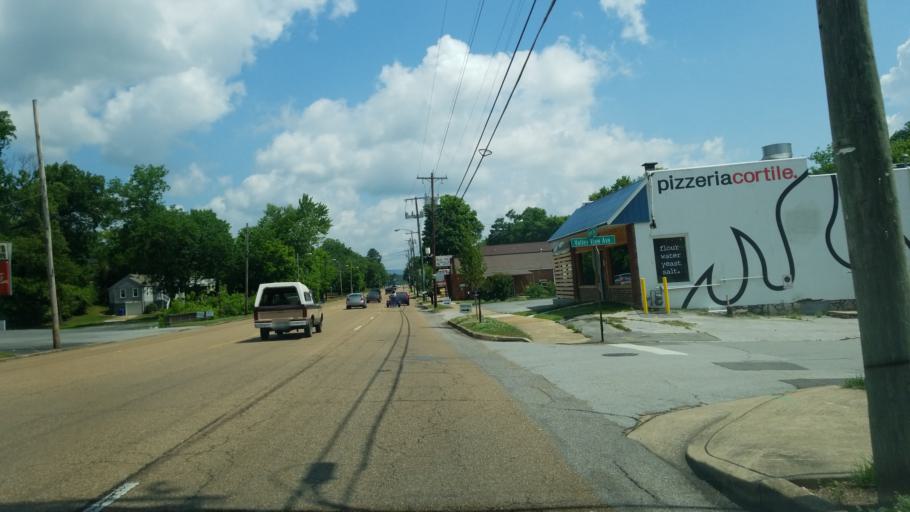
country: US
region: Tennessee
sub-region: Hamilton County
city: Red Bank
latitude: 35.1265
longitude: -85.2847
